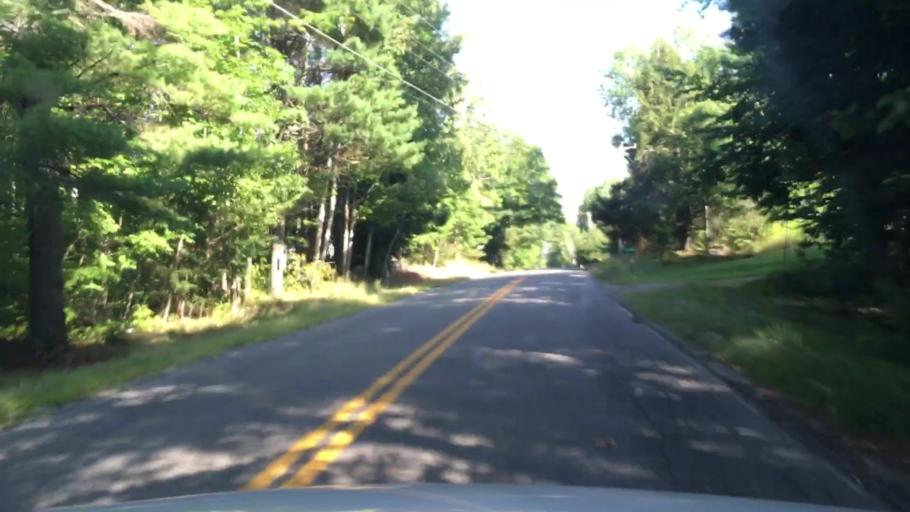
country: US
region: Maine
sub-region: Penobscot County
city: Enfield
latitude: 45.2403
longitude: -68.5610
